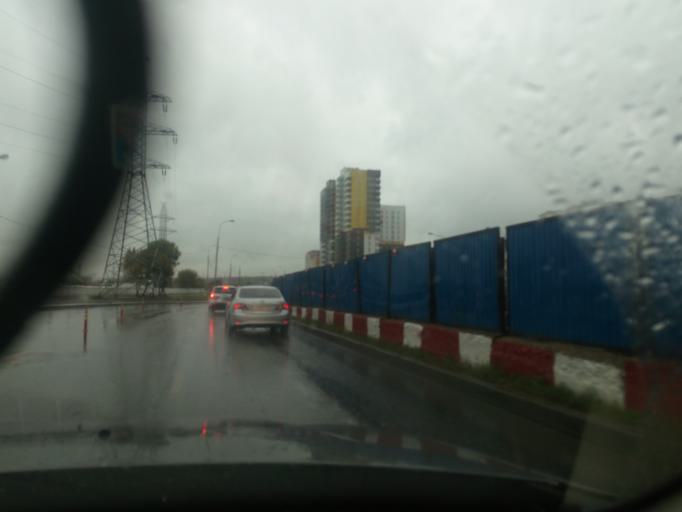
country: RU
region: Moscow
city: Zhulebino
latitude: 55.7104
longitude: 37.8774
